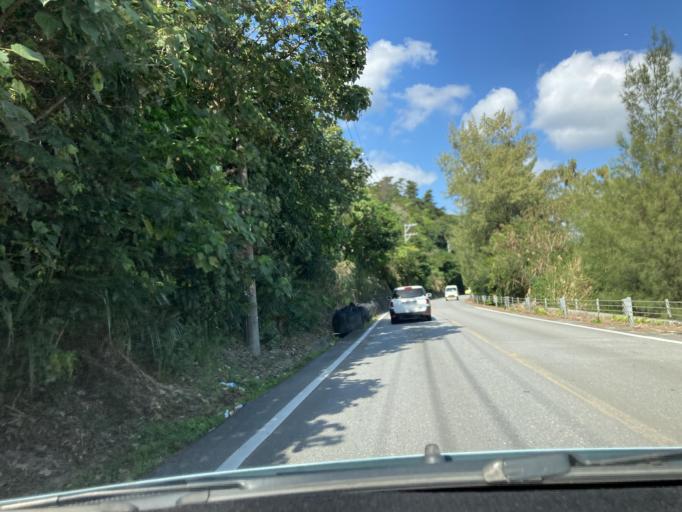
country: JP
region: Okinawa
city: Nago
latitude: 26.6382
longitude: 128.0031
